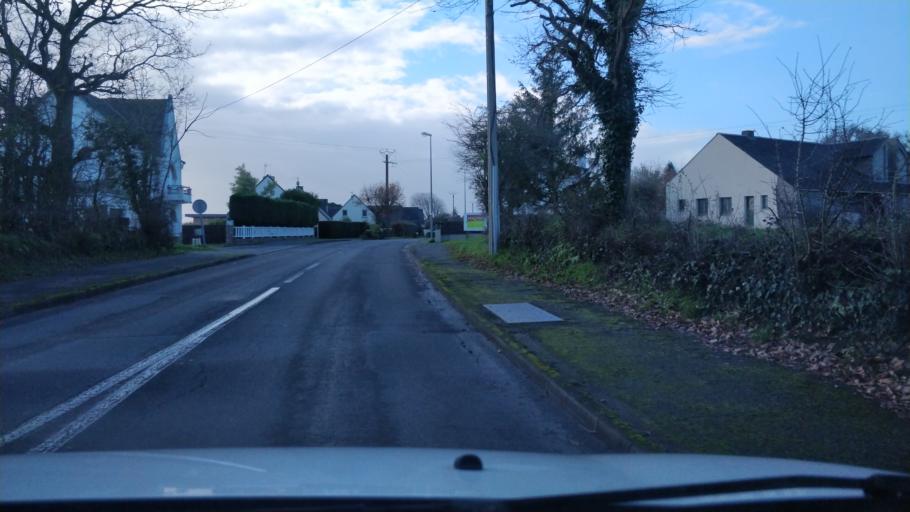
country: FR
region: Pays de la Loire
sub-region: Departement de la Loire-Atlantique
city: Asserac
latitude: 47.4267
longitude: -2.3933
